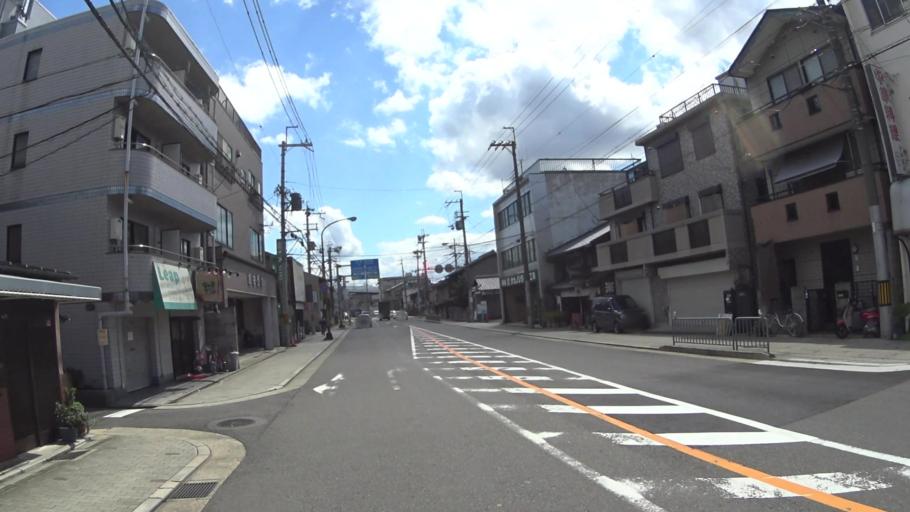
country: JP
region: Kyoto
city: Kyoto
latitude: 34.9743
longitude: 135.7618
